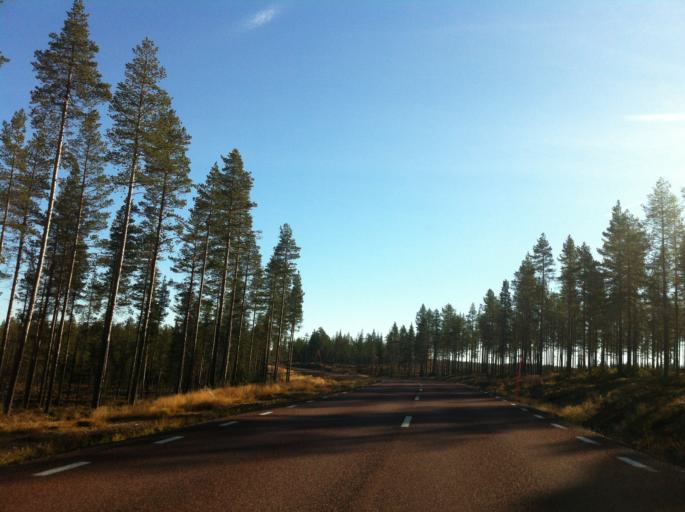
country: SE
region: Dalarna
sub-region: Alvdalens Kommun
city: AElvdalen
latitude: 61.6359
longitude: 13.2163
